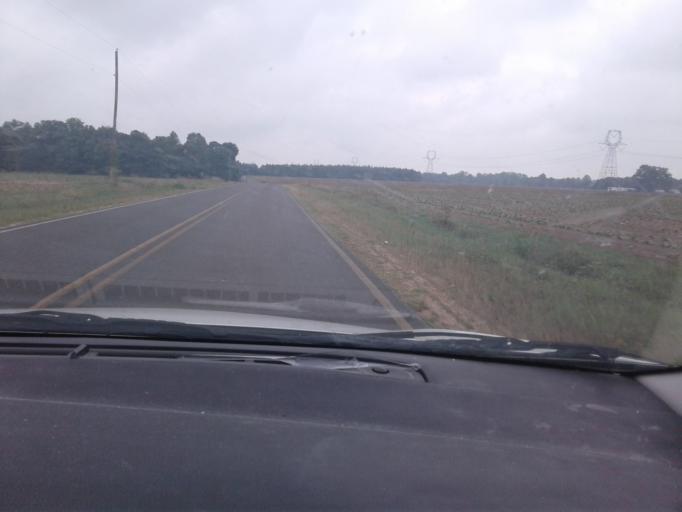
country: US
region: North Carolina
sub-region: Harnett County
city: Coats
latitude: 35.3718
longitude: -78.6479
